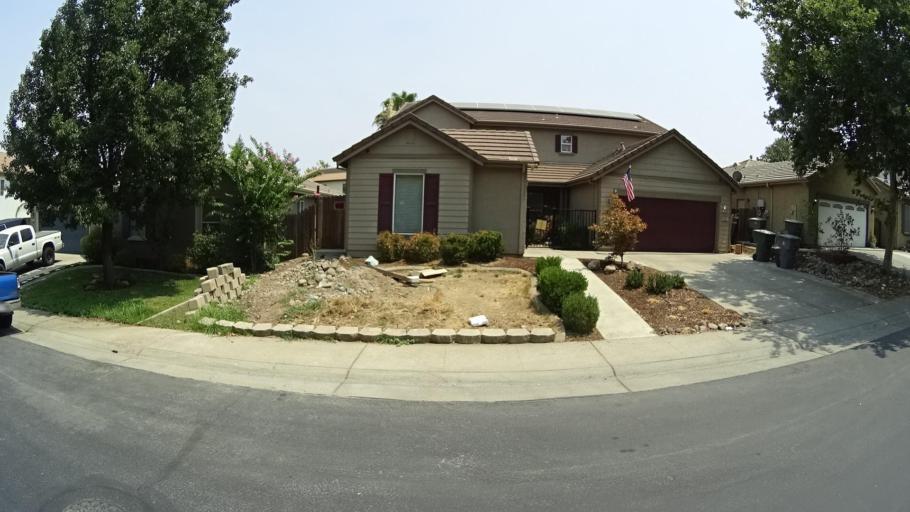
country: US
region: California
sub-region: Placer County
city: Rocklin
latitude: 38.7967
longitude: -121.2791
